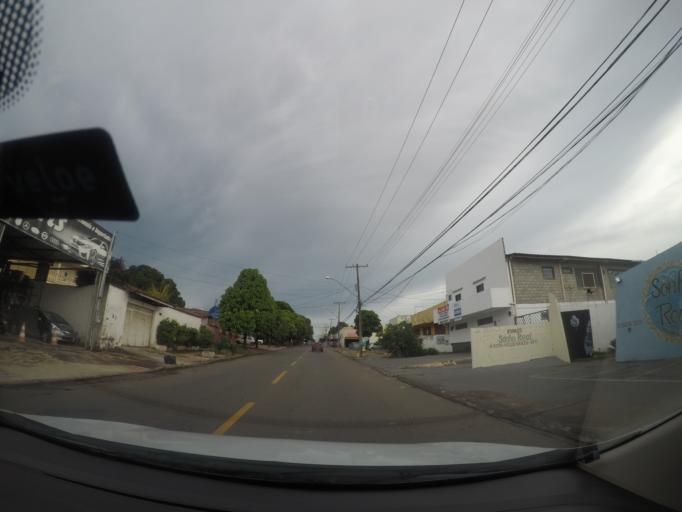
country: BR
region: Goias
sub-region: Goiania
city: Goiania
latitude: -16.6992
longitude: -49.3077
